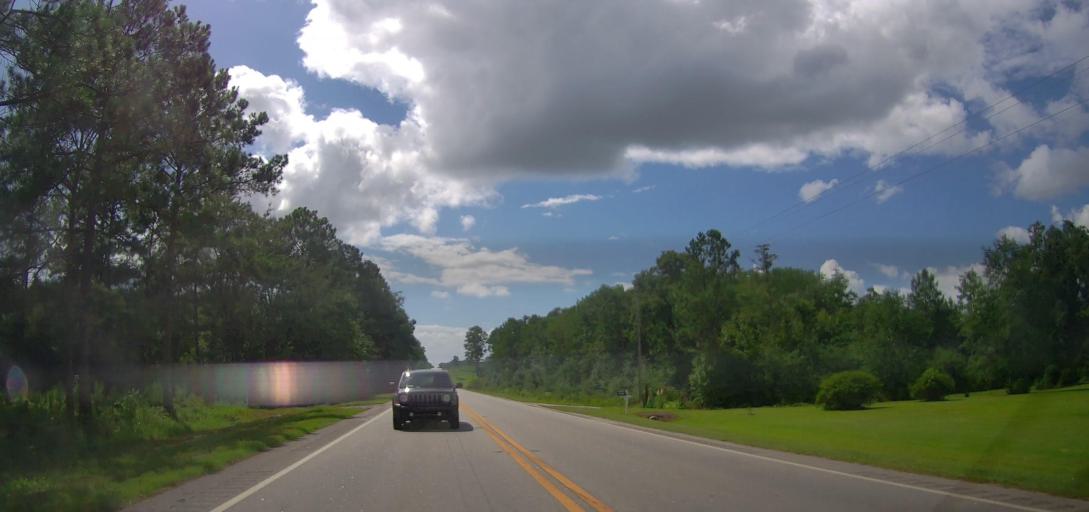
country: US
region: Georgia
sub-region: Coffee County
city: Broxton
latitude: 31.5600
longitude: -82.9809
